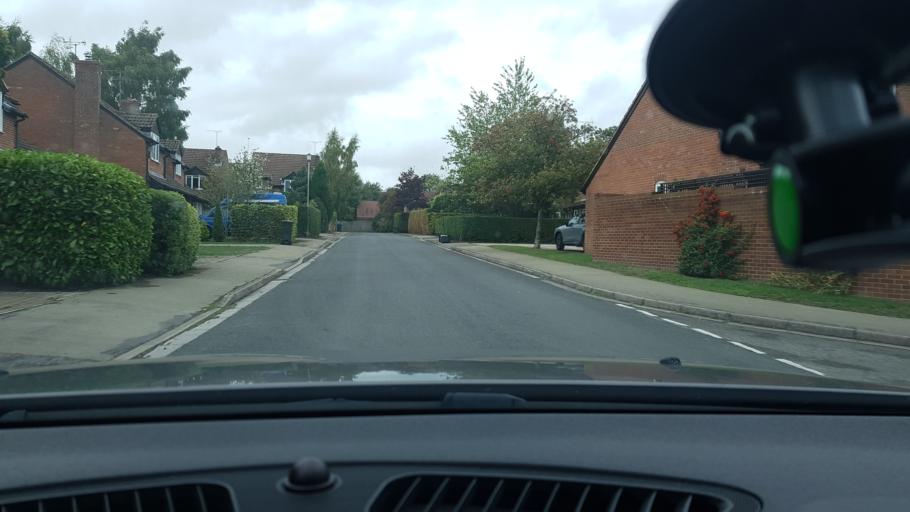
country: GB
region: England
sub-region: Wiltshire
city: Burbage
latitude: 51.3507
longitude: -1.6695
